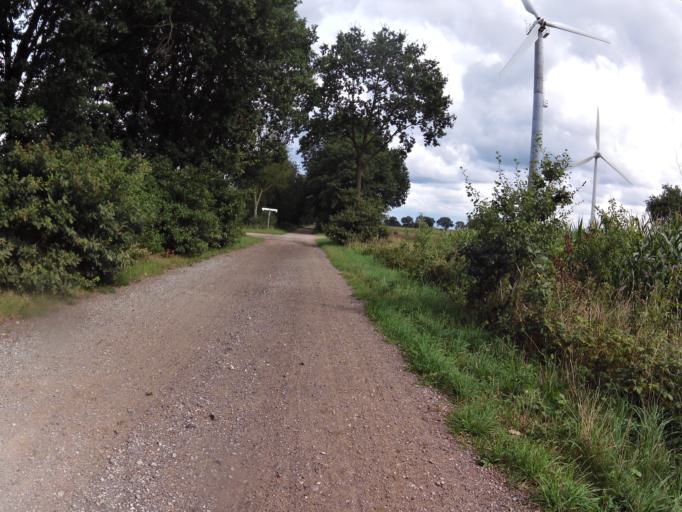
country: DE
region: Lower Saxony
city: Oerel
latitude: 53.4932
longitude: 9.0537
